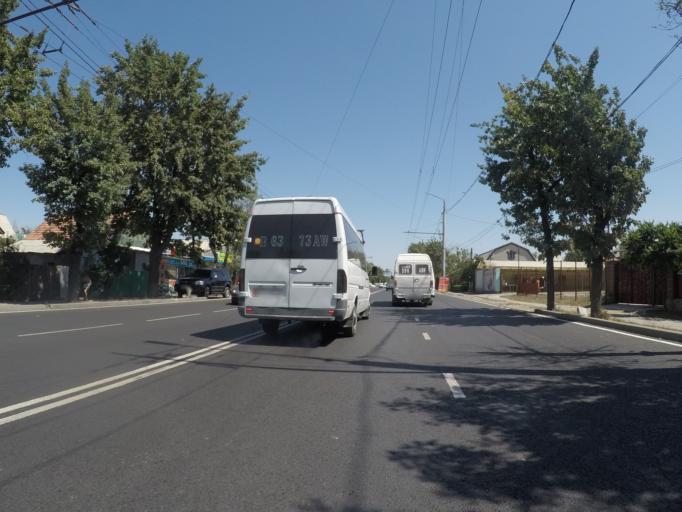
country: KG
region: Chuy
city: Bishkek
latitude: 42.8437
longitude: 74.5778
